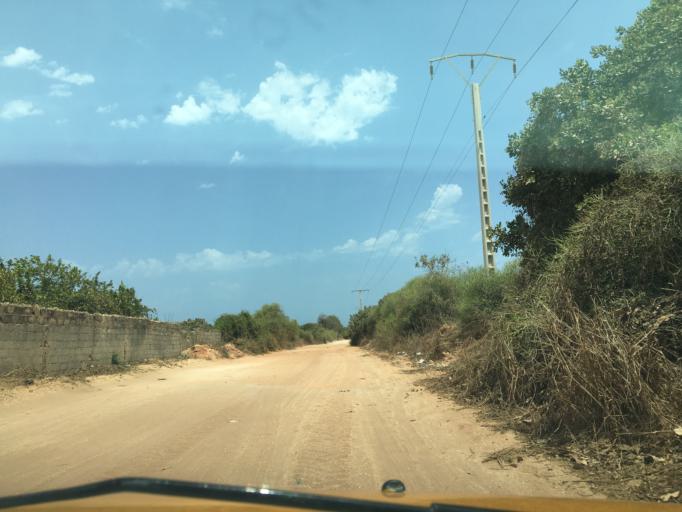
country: SN
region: Thies
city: Thies
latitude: 14.8153
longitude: -17.1948
